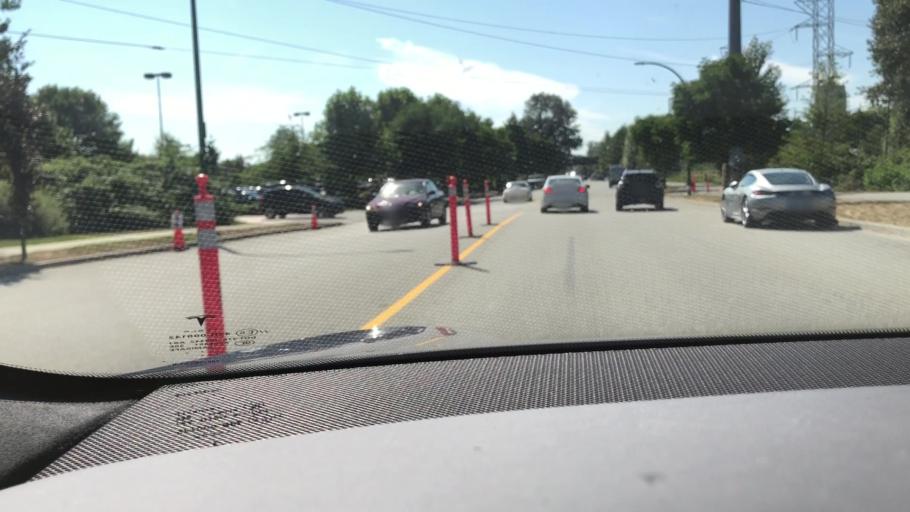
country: CA
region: British Columbia
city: Burnaby
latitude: 49.2611
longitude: -122.9992
